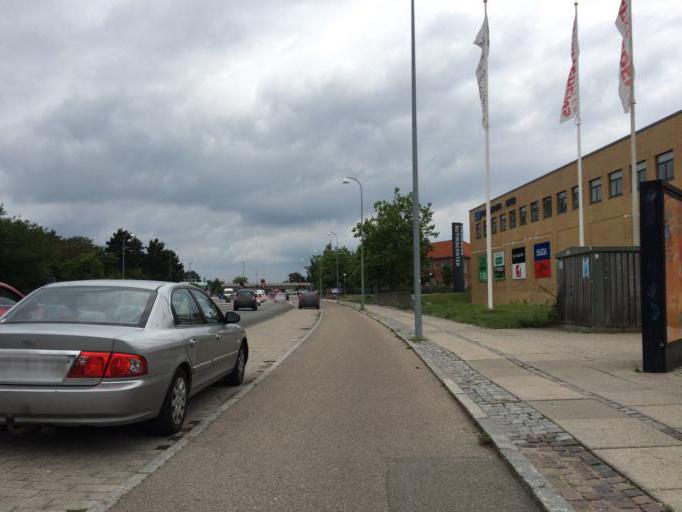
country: DK
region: Capital Region
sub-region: Hvidovre Kommune
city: Hvidovre
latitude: 55.6262
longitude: 12.4825
